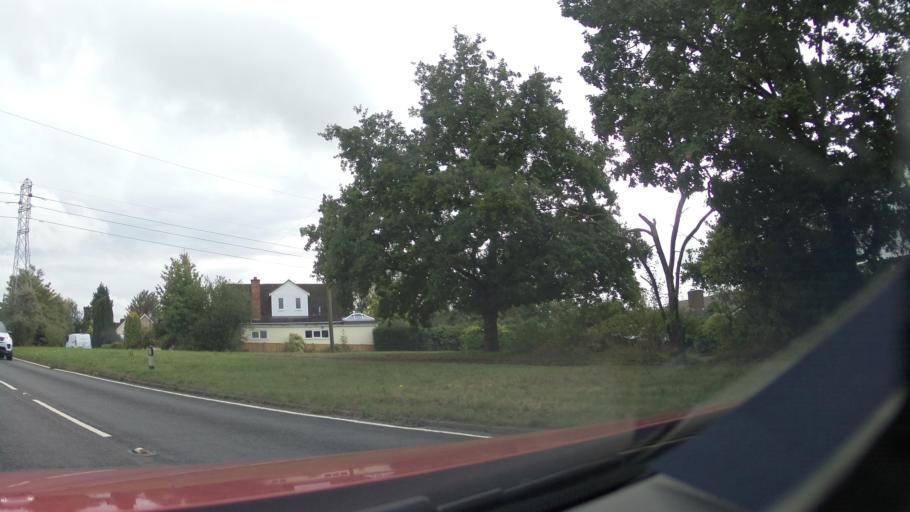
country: GB
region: England
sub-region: Worcestershire
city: Droitwich
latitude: 52.3143
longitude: -2.1773
